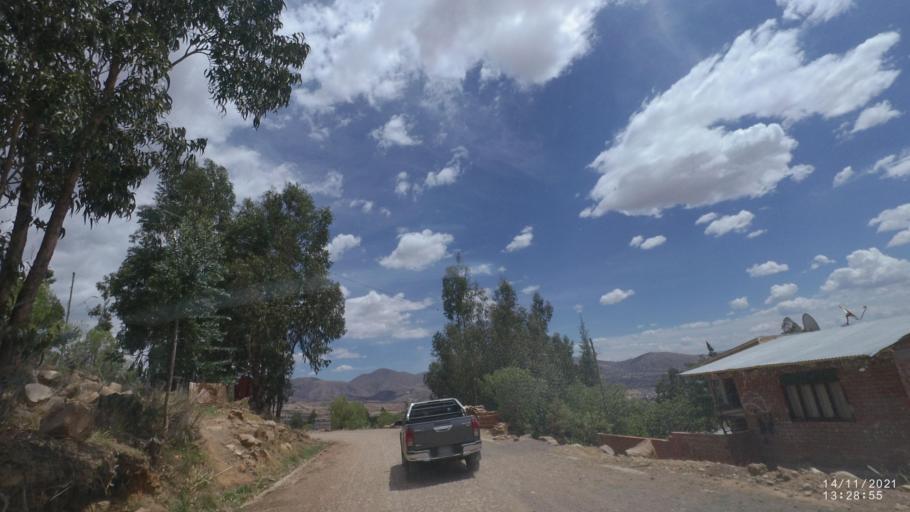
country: BO
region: Cochabamba
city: Colomi
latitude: -17.3869
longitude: -65.9852
